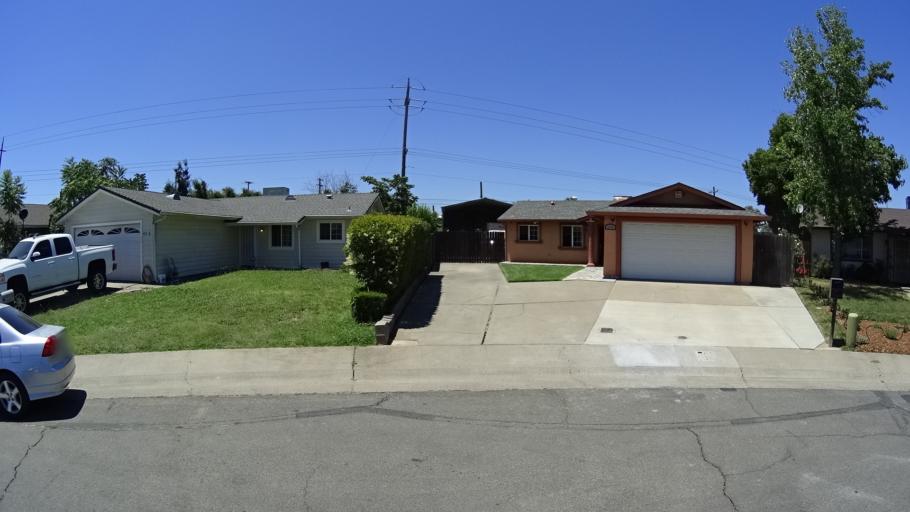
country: US
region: California
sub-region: Sacramento County
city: Parkway
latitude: 38.5354
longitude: -121.4823
